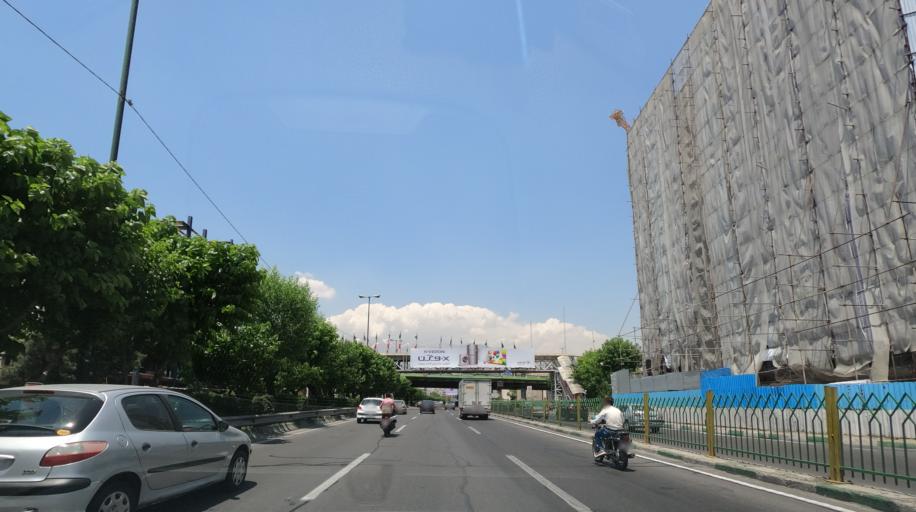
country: IR
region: Tehran
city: Tajrish
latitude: 35.7607
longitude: 51.4207
